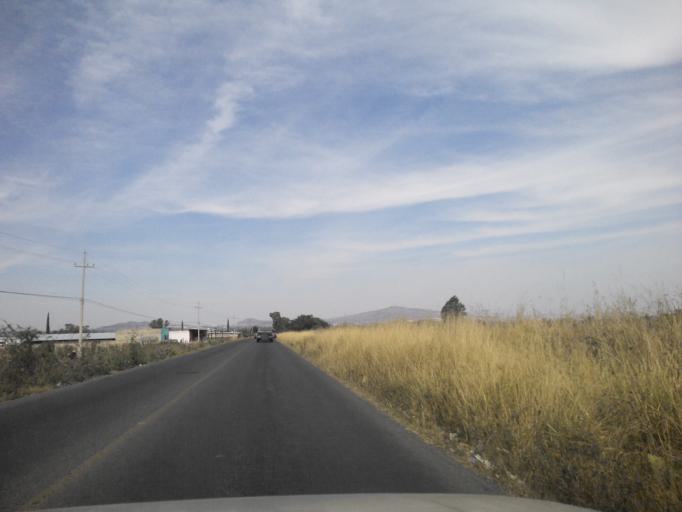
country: MX
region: Jalisco
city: San Sebastian el Grande
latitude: 20.5082
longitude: -103.4134
